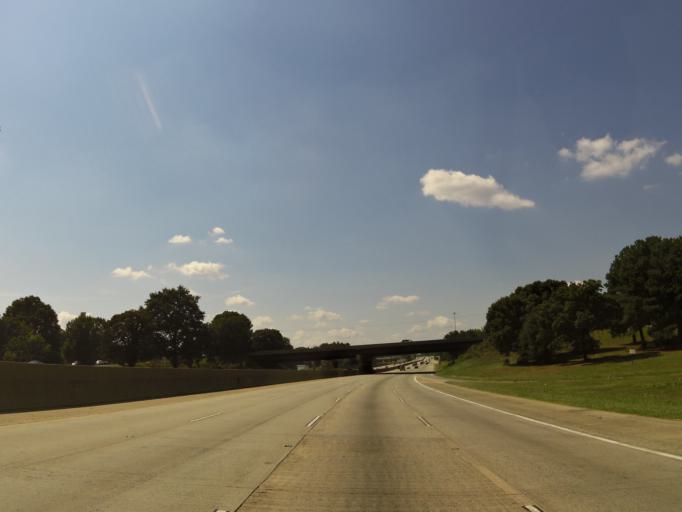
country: US
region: North Carolina
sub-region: Mecklenburg County
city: Charlotte
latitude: 35.2382
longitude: -80.9179
